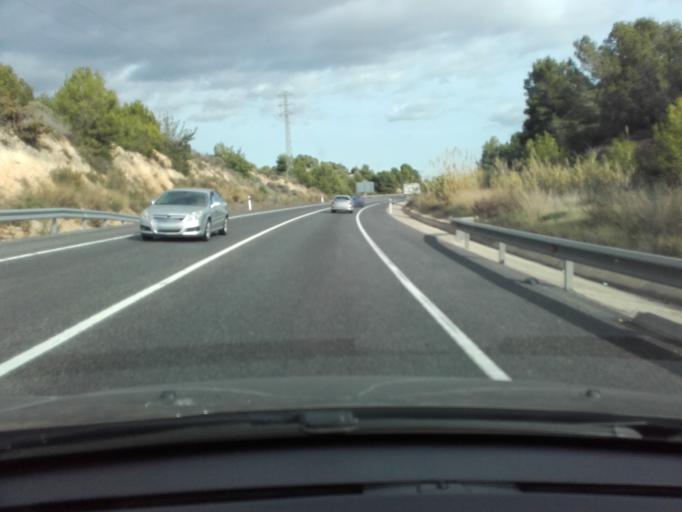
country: ES
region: Catalonia
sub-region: Provincia de Tarragona
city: Altafulla
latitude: 41.1455
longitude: 1.3529
